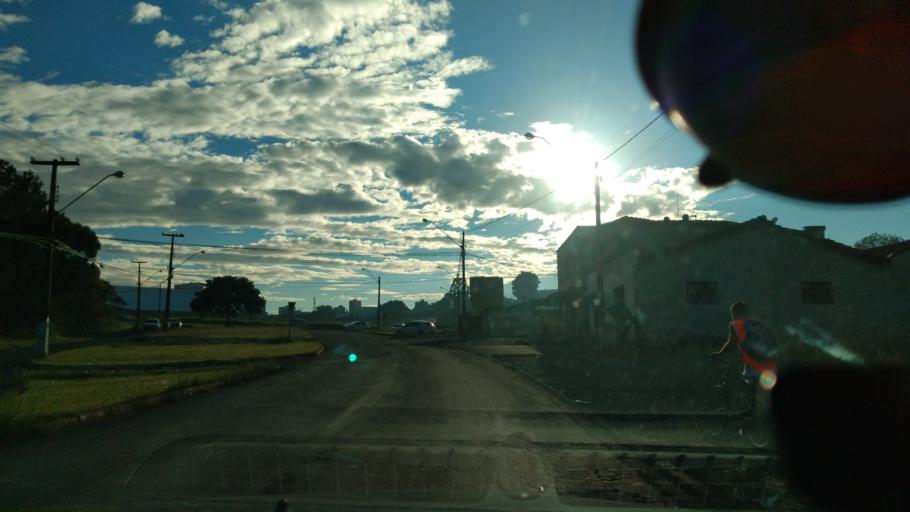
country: BR
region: Parana
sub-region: Guarapuava
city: Guarapuava
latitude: -25.3943
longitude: -51.4830
